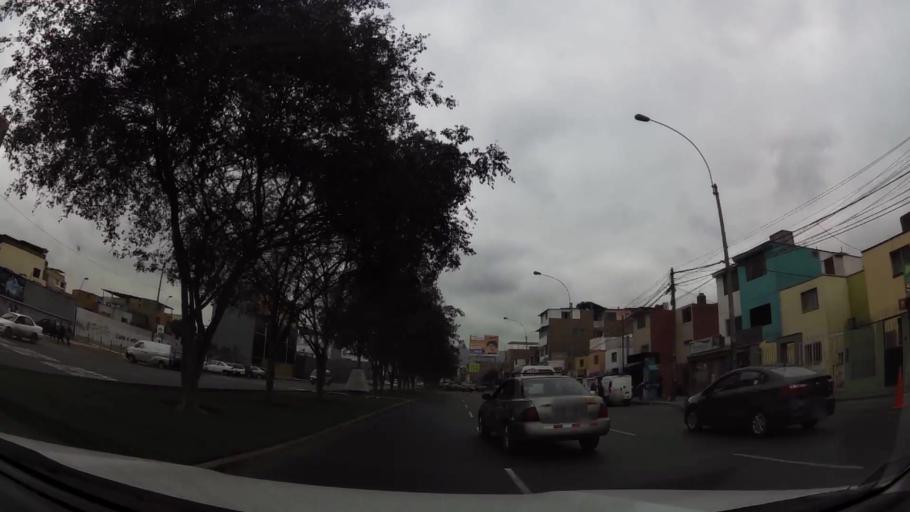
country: PE
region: Lima
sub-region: Lima
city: Surco
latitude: -12.1507
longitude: -76.9882
